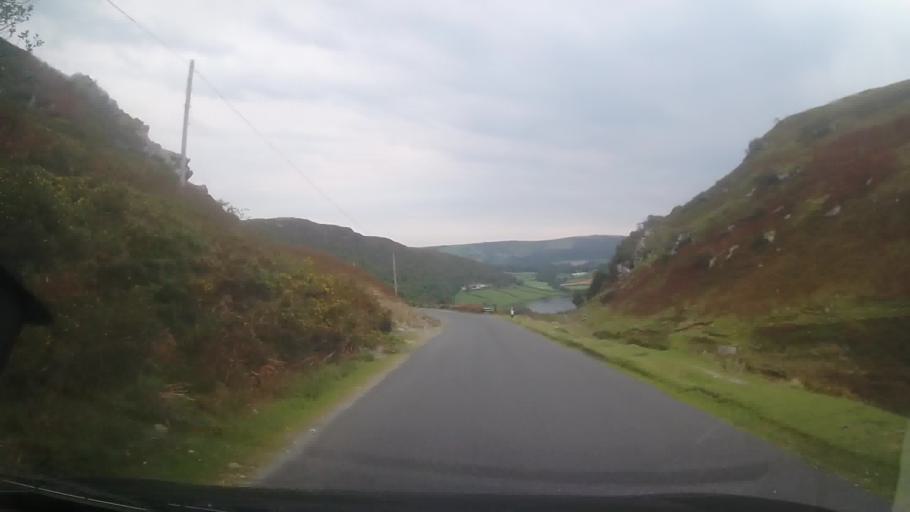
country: GB
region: Wales
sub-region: Sir Powys
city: Rhayader
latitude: 52.3142
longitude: -3.5585
